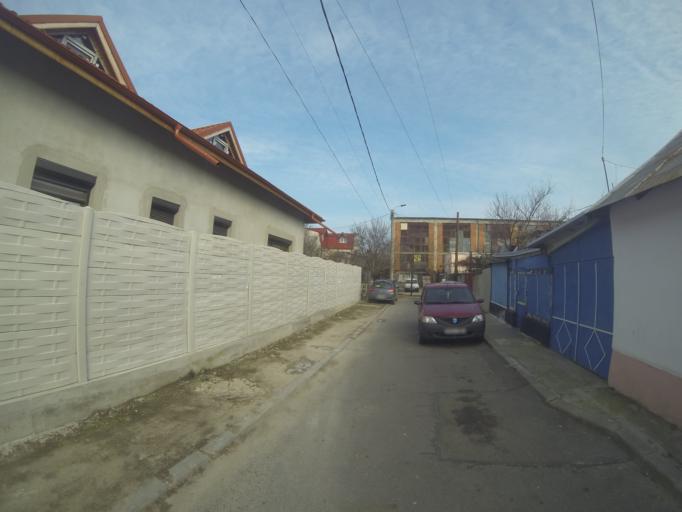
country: RO
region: Bucuresti
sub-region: Municipiul Bucuresti
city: Bucuresti
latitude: 44.4033
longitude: 26.0848
